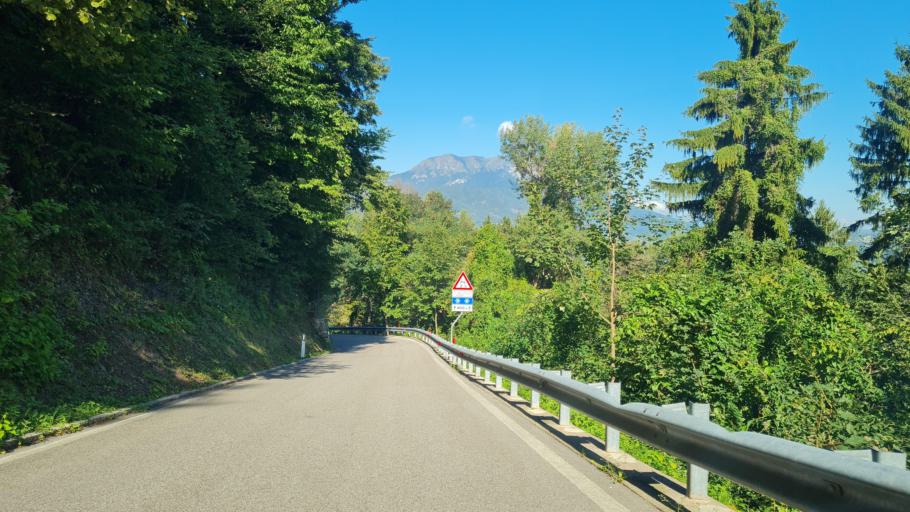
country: IT
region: Trentino-Alto Adige
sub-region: Provincia di Trento
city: Caldonazzo
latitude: 45.9821
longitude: 11.2865
